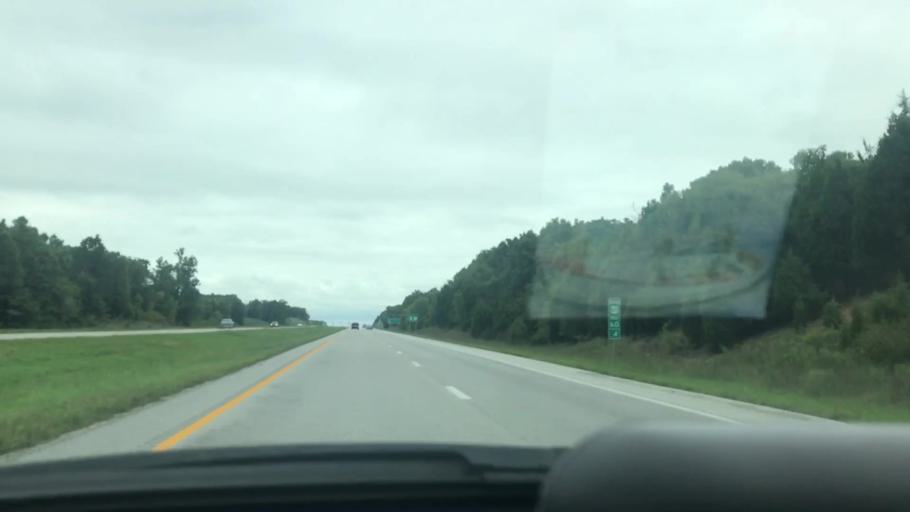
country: US
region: Missouri
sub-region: Greene County
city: Fair Grove
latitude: 37.3227
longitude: -93.1678
